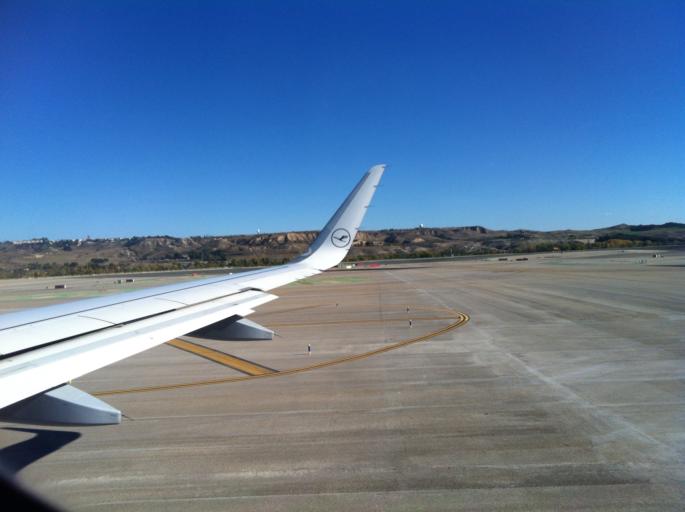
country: ES
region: Madrid
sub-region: Provincia de Madrid
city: Barajas de Madrid
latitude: 40.4944
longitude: -3.5625
